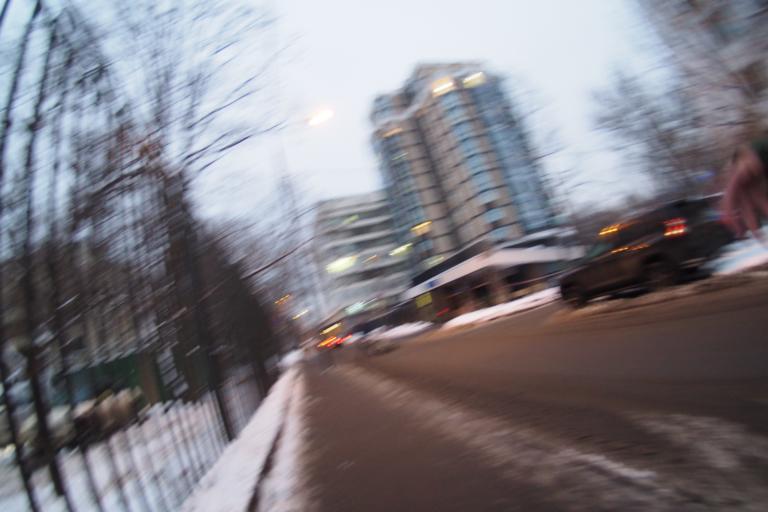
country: RU
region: Moscow
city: Sokol
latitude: 55.8017
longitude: 37.5596
